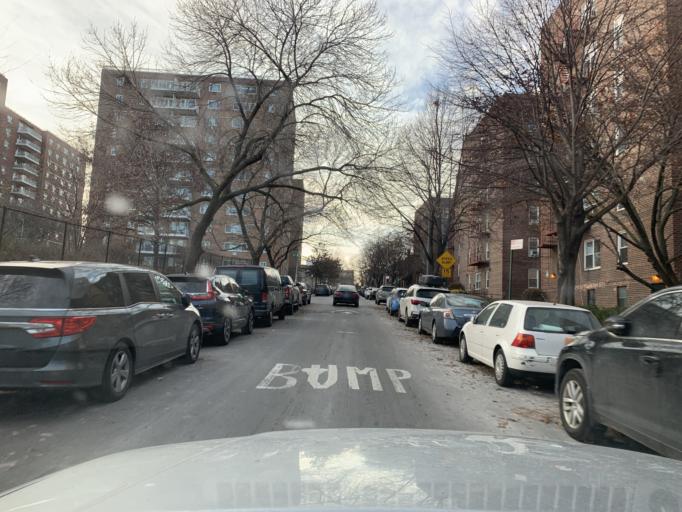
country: US
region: New York
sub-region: Queens County
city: Long Island City
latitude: 40.7479
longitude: -73.9119
